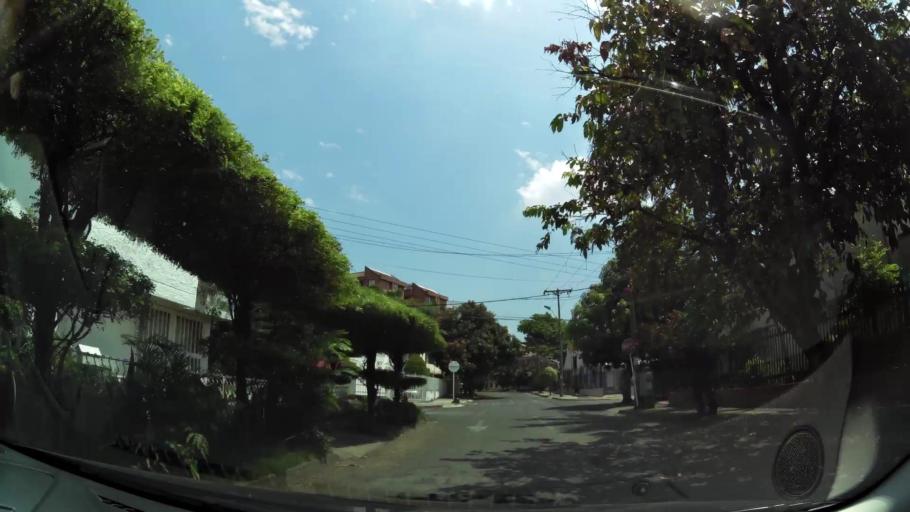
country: CO
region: Valle del Cauca
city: Cali
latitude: 3.4146
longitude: -76.5431
